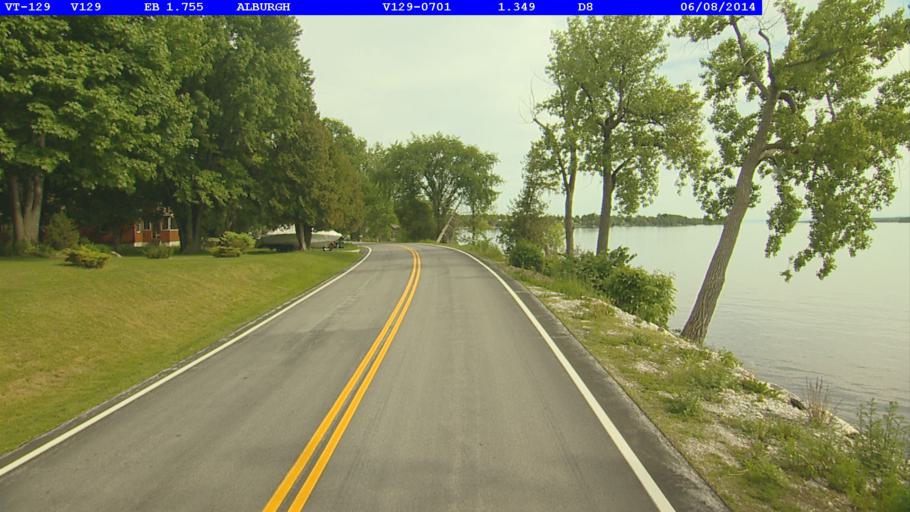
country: US
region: Vermont
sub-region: Grand Isle County
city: North Hero
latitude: 44.8917
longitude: -73.3047
